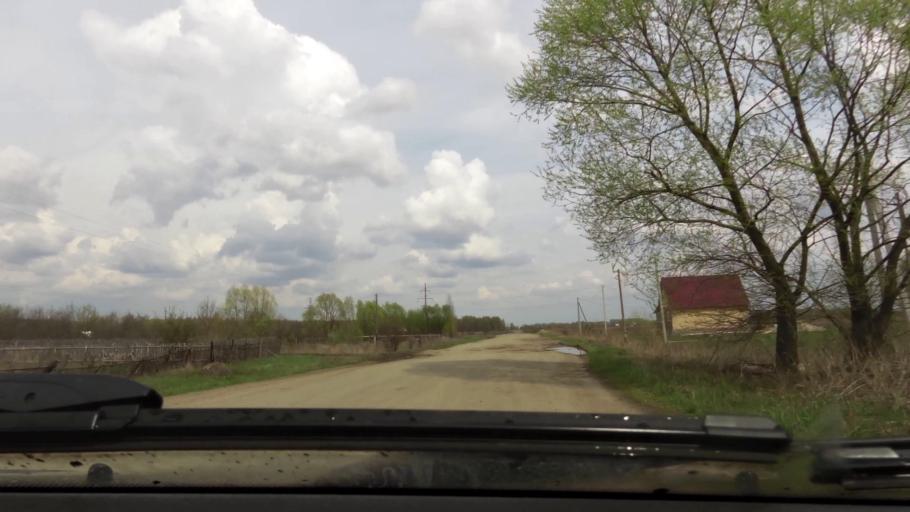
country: RU
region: Rjazan
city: Bagramovo
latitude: 54.6998
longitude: 39.3082
